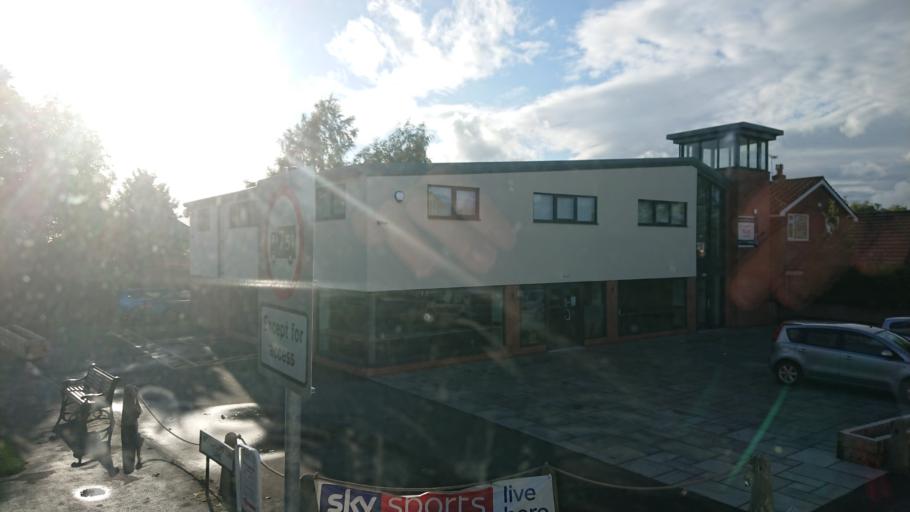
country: GB
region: England
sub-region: Lancashire
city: Preston
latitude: 53.8100
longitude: -2.7236
